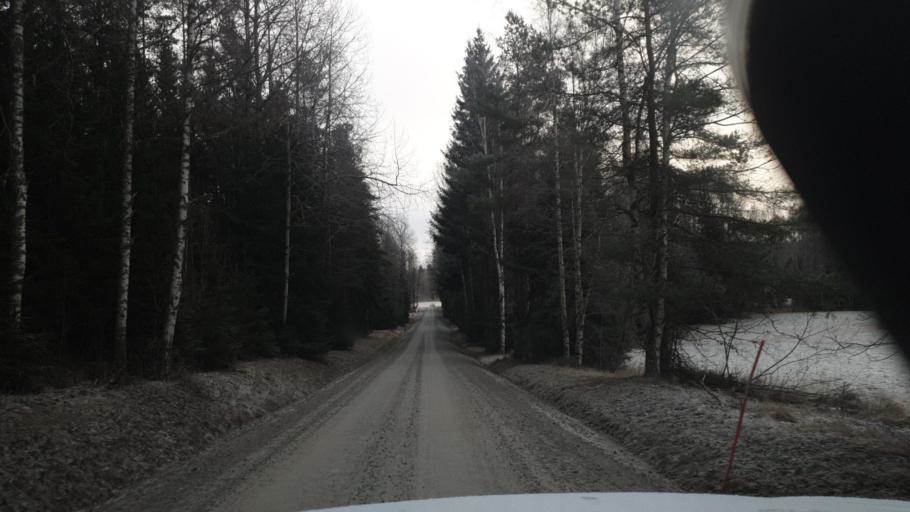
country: SE
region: Vaermland
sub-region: Karlstads Kommun
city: Edsvalla
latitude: 59.5152
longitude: 13.0124
